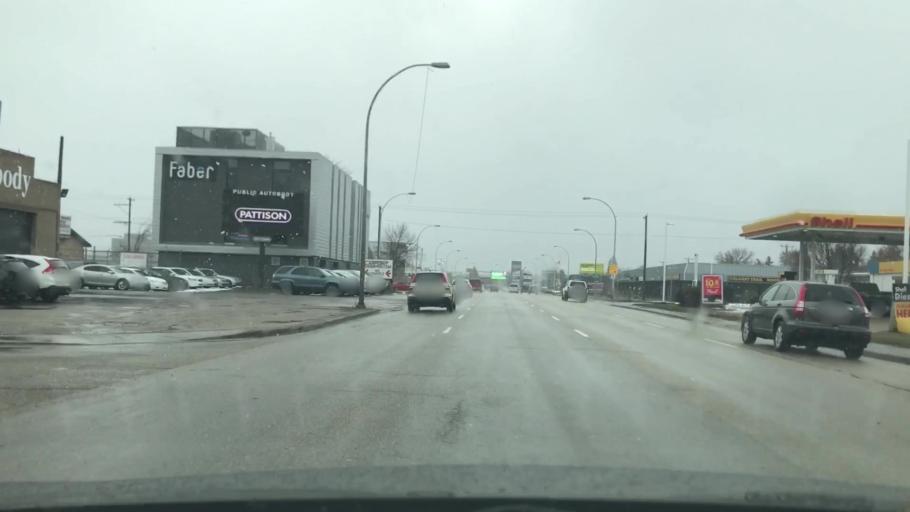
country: CA
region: Alberta
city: Edmonton
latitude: 53.4961
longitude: -113.4977
